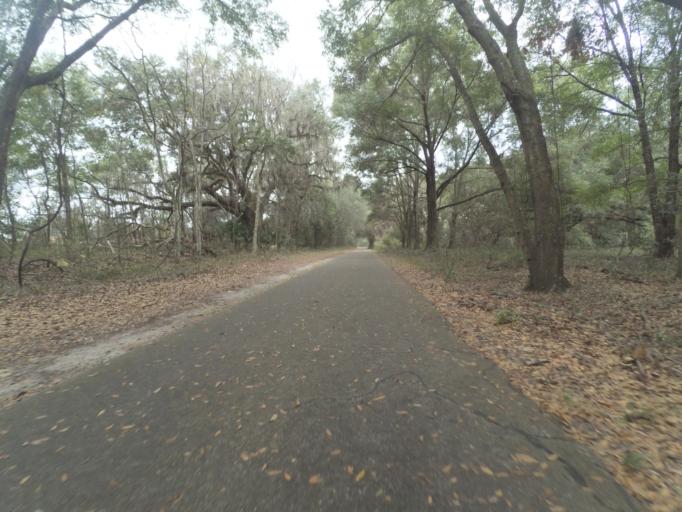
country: US
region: Florida
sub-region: Alachua County
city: Gainesville
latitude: 29.6096
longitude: -82.3054
